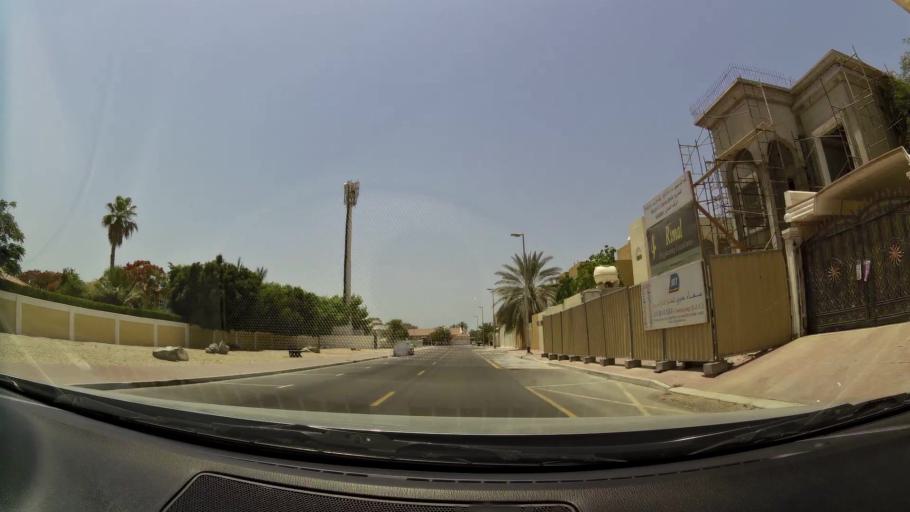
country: AE
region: Dubai
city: Dubai
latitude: 25.2009
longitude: 55.2448
